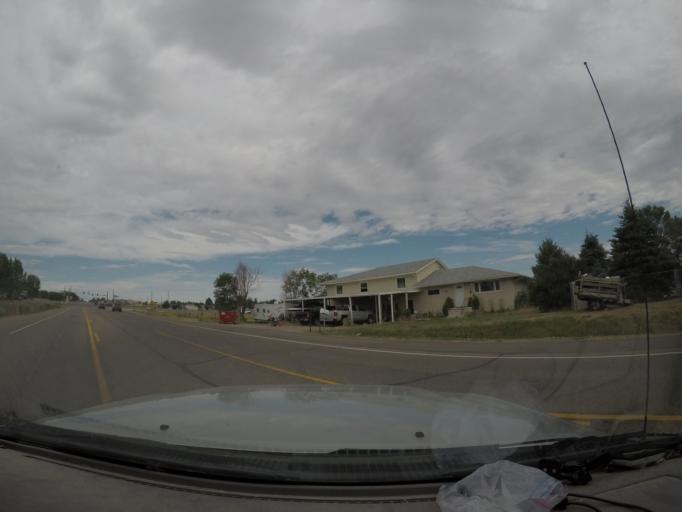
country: US
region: Wyoming
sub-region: Laramie County
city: Fox Farm-College
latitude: 41.1454
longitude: -104.7535
